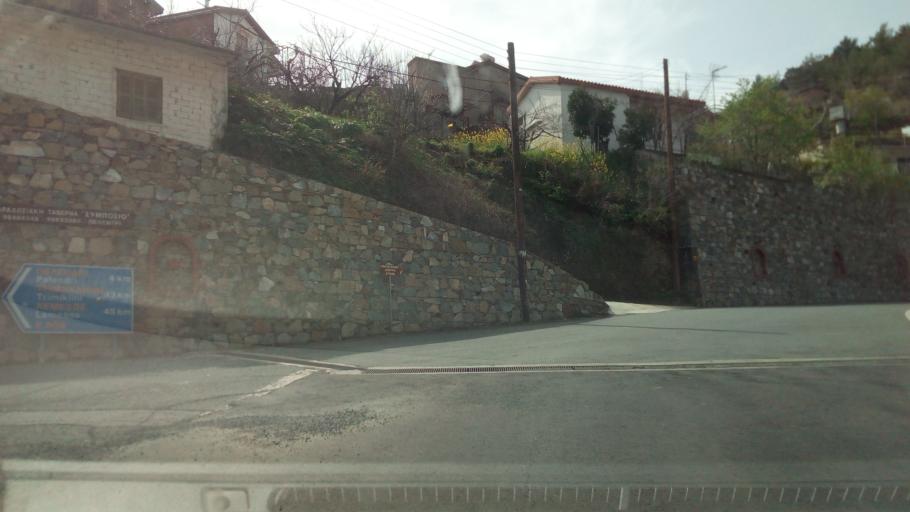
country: CY
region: Limassol
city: Pelendri
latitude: 34.9075
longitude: 32.9898
